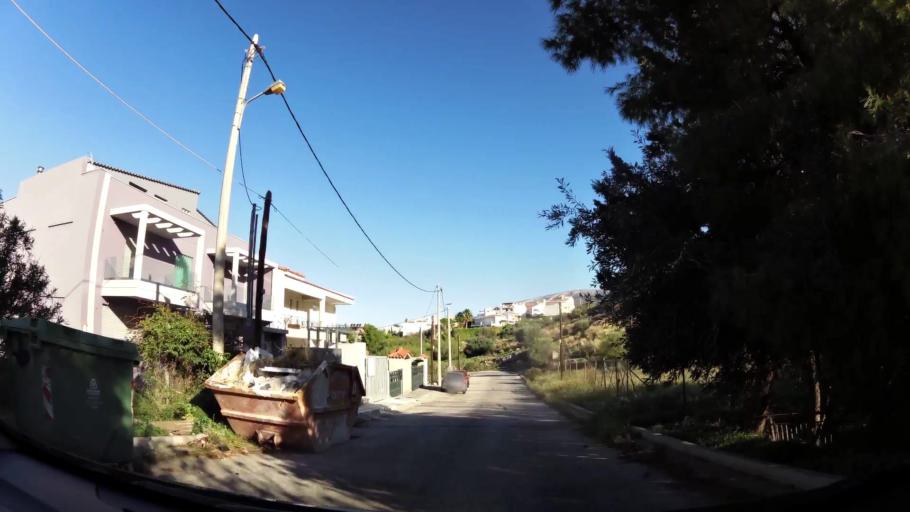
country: GR
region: Attica
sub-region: Nomarchia Athinas
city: Glyfada
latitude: 37.8775
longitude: 23.7723
